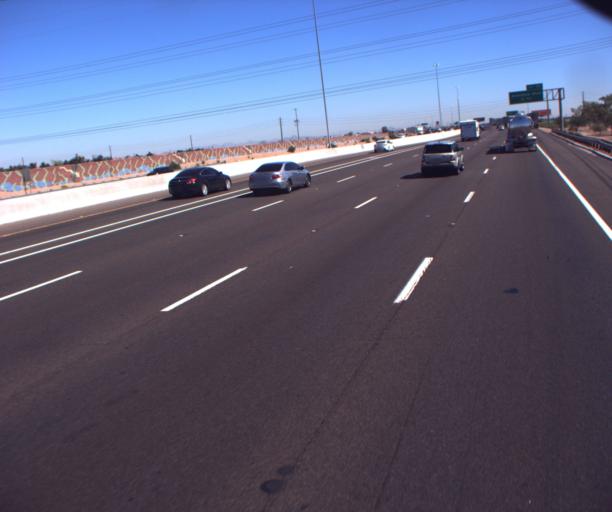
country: US
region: Arizona
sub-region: Maricopa County
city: Avondale
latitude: 33.4575
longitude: -112.3203
